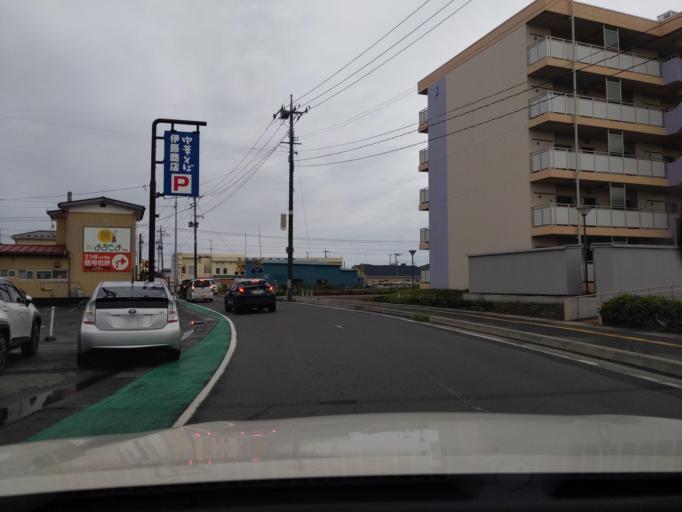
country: JP
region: Miyagi
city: Ishinomaki
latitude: 38.4375
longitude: 141.2644
